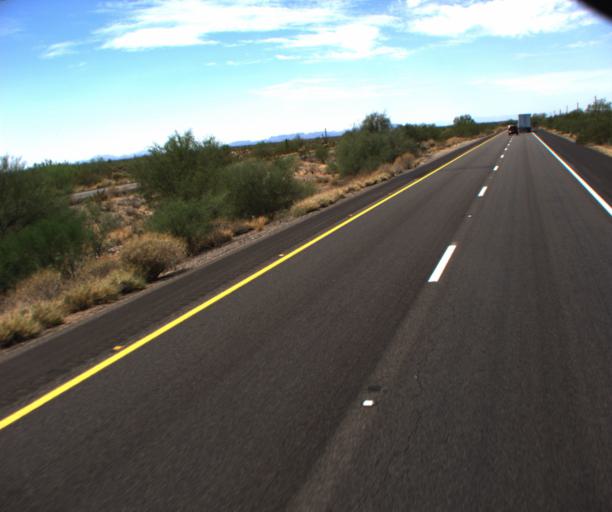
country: US
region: Arizona
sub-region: Pinal County
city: Gold Camp
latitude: 33.2578
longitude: -111.3103
